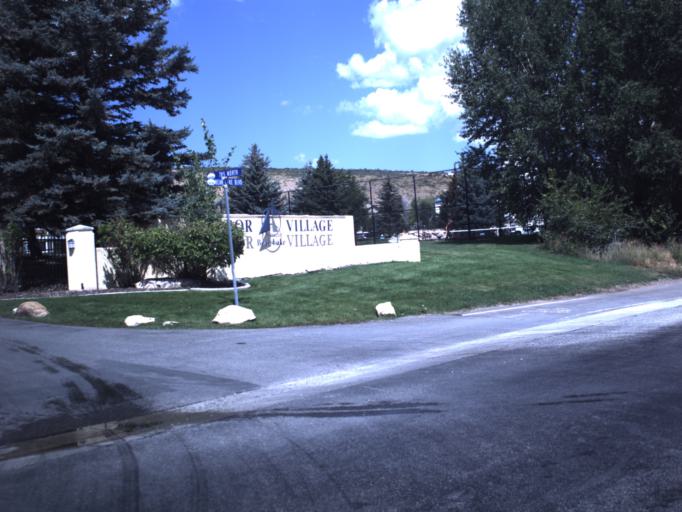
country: US
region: Idaho
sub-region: Bear Lake County
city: Paris
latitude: 41.9608
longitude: -111.4006
